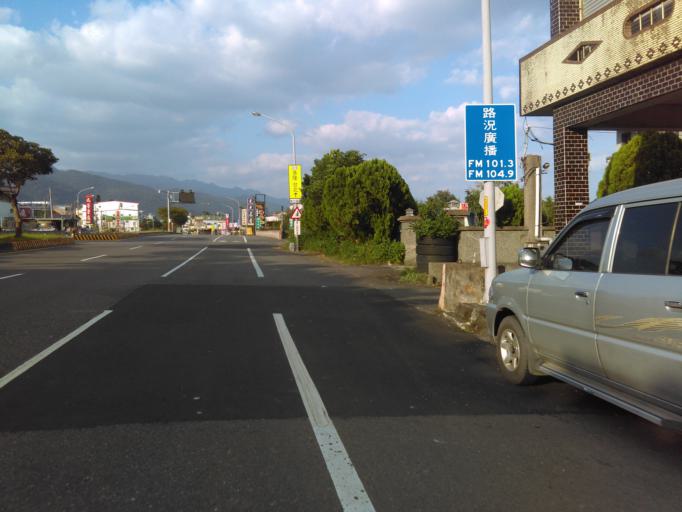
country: TW
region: Taiwan
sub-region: Yilan
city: Yilan
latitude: 24.8069
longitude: 121.7664
